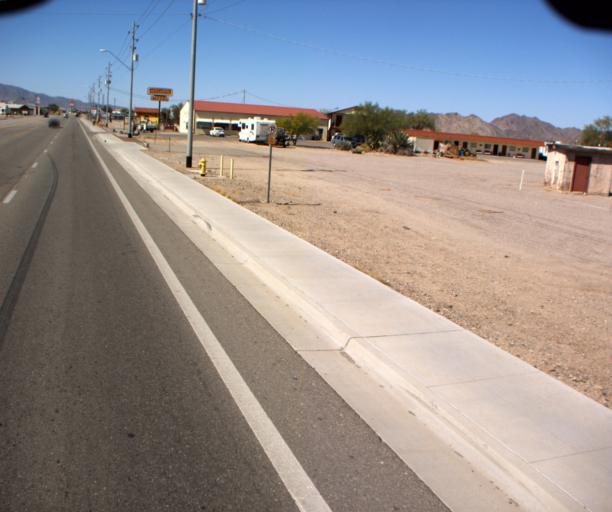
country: US
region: Arizona
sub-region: La Paz County
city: Quartzsite
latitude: 33.6639
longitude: -114.2307
